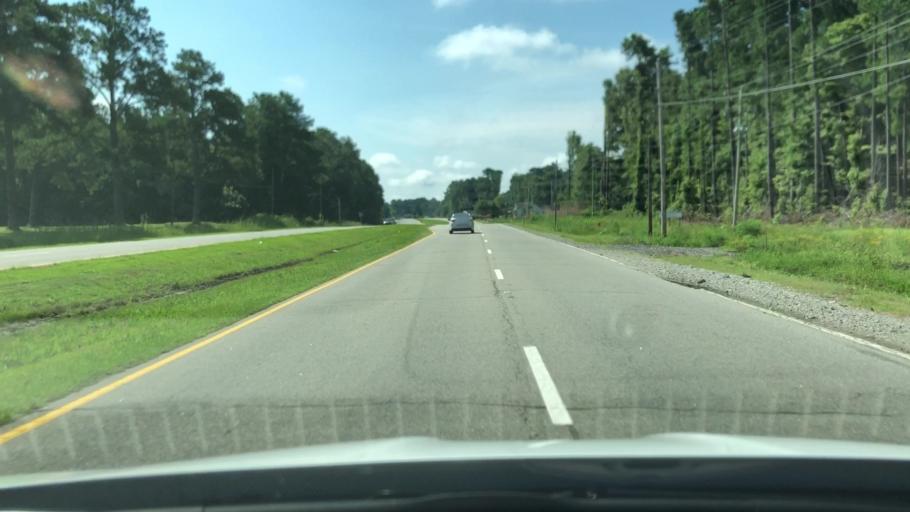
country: US
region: North Carolina
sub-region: Bertie County
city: Windsor
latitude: 35.9716
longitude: -76.9552
